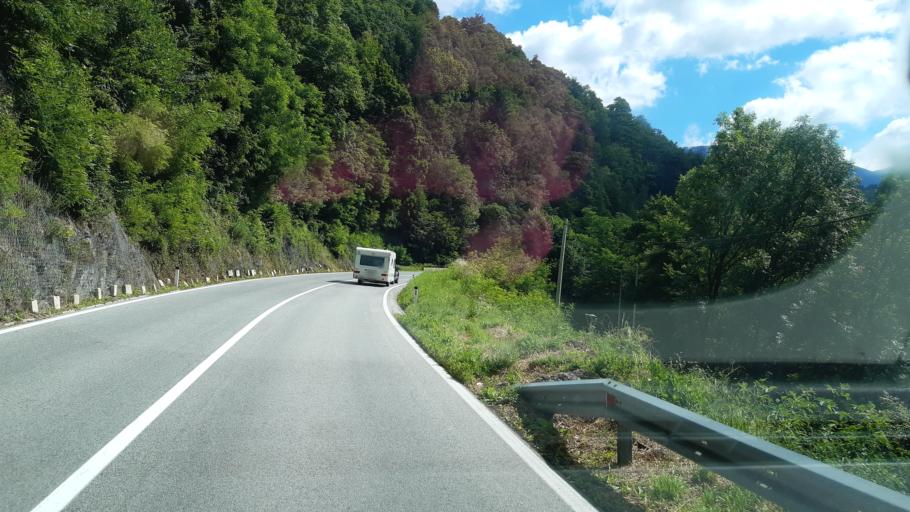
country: SI
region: Trzic
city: Trzic
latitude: 46.3616
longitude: 14.3017
